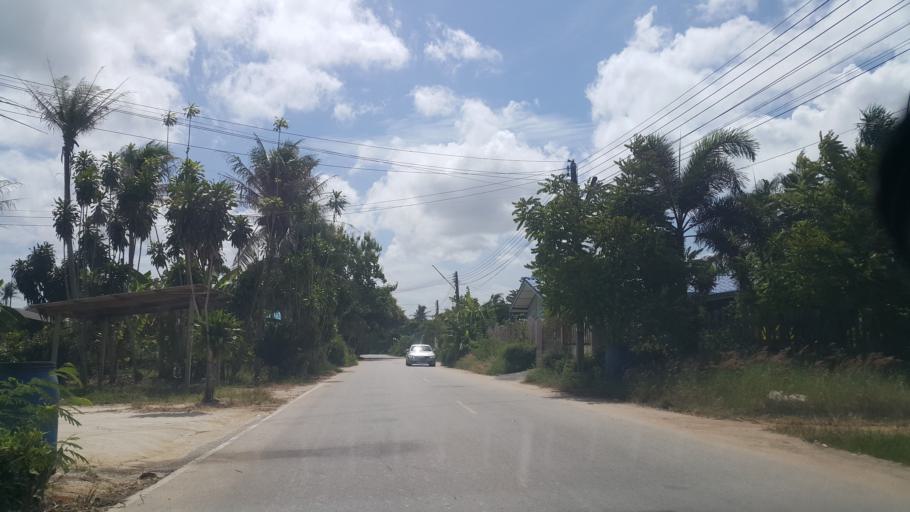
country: TH
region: Rayong
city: Ban Chang
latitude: 12.7983
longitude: 101.0250
